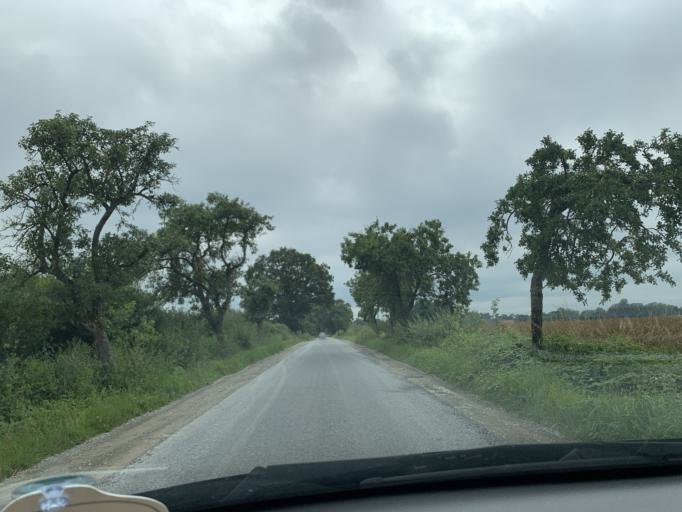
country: DE
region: North Rhine-Westphalia
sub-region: Regierungsbezirk Munster
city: Ennigerloh
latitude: 51.8365
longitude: 8.0764
